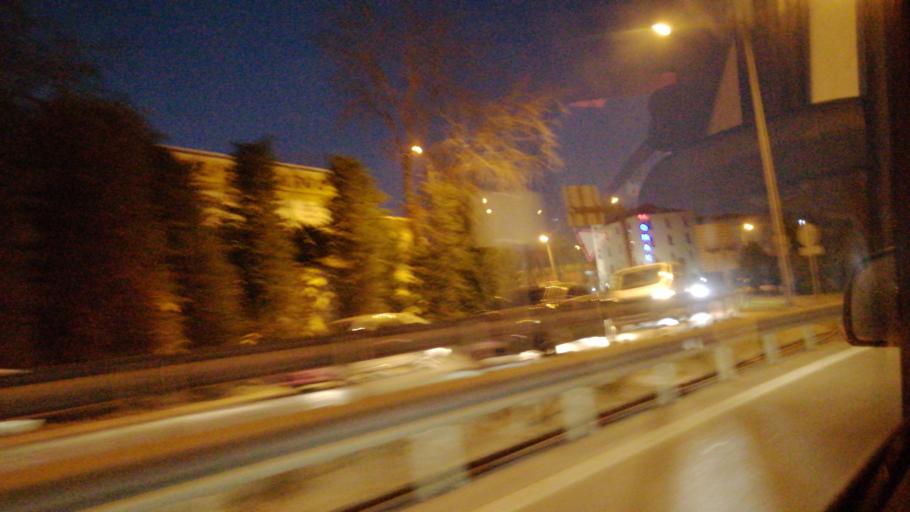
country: TR
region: Istanbul
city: Umraniye
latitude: 40.9955
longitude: 29.1543
